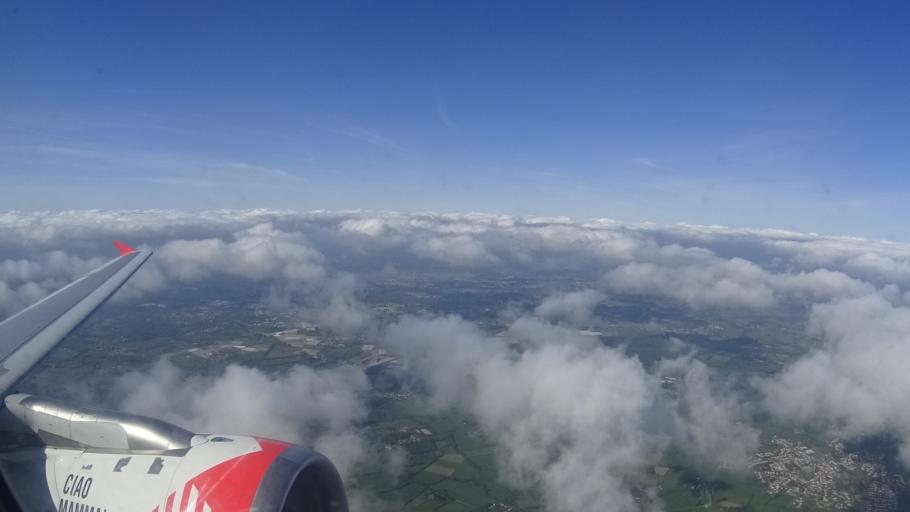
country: FR
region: Pays de la Loire
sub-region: Departement de la Loire-Atlantique
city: Geneston
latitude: 47.0778
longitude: -1.5309
